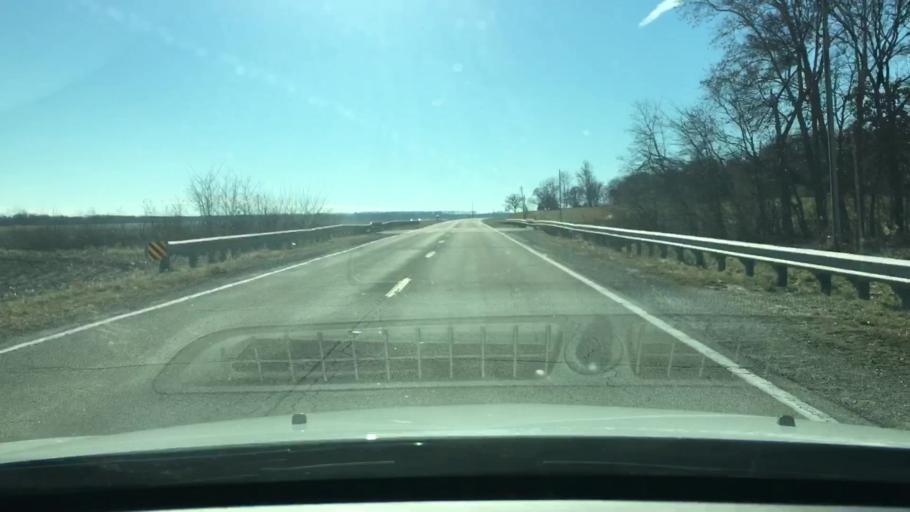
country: US
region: Illinois
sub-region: Mason County
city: Havana
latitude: 40.2625
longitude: -90.1776
